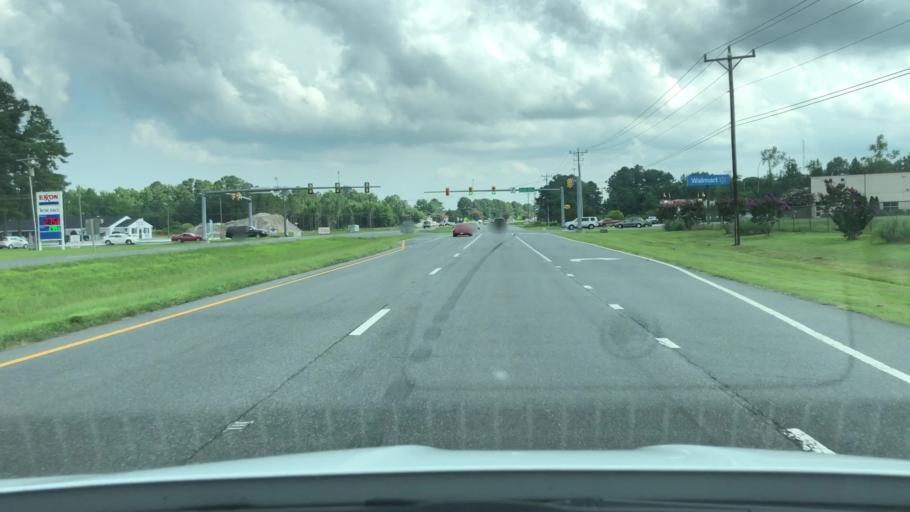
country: US
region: Virginia
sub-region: Accomack County
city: Onancock
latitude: 37.6848
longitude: -75.7226
